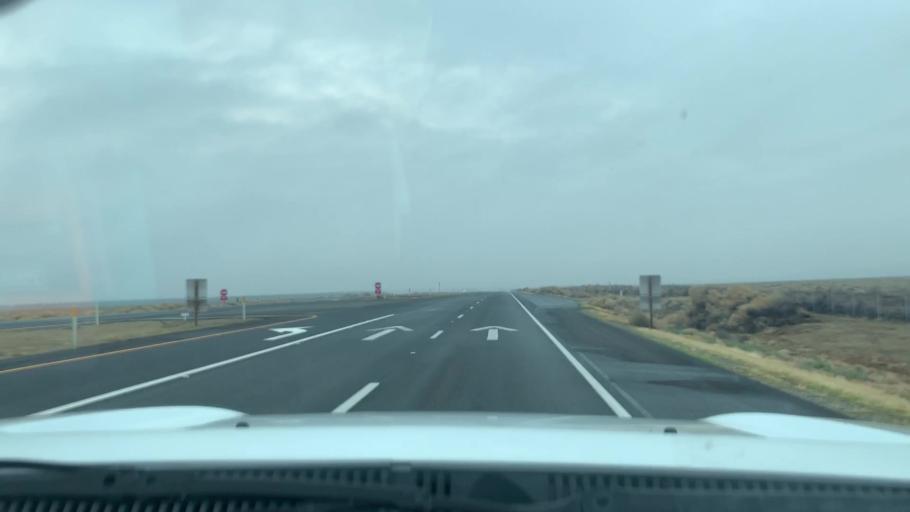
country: US
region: California
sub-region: Kern County
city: Lost Hills
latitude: 35.6322
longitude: -120.0020
